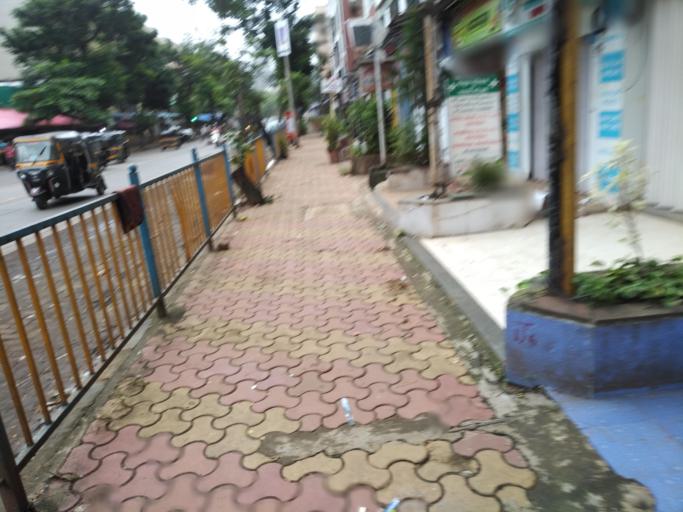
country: IN
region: Maharashtra
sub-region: Mumbai Suburban
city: Borivli
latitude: 19.2347
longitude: 72.8641
